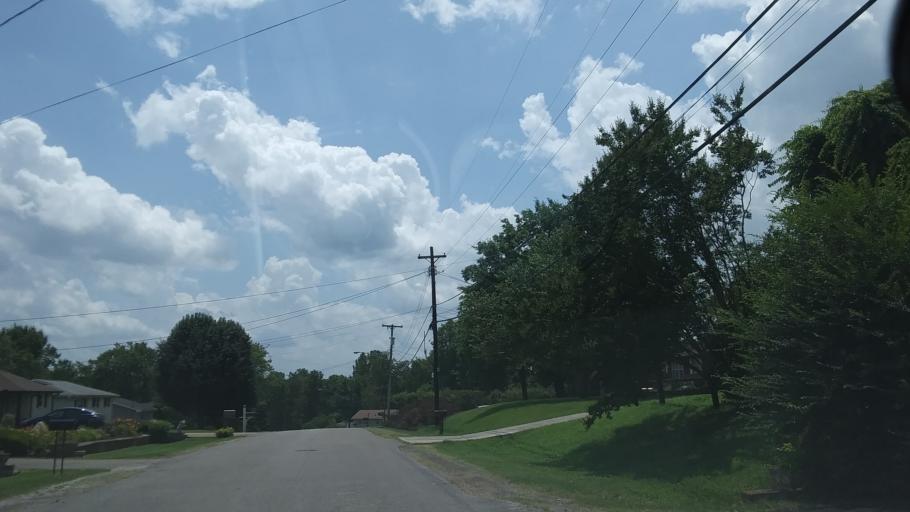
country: US
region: Tennessee
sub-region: Davidson County
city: Belle Meade
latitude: 36.1527
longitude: -86.8869
